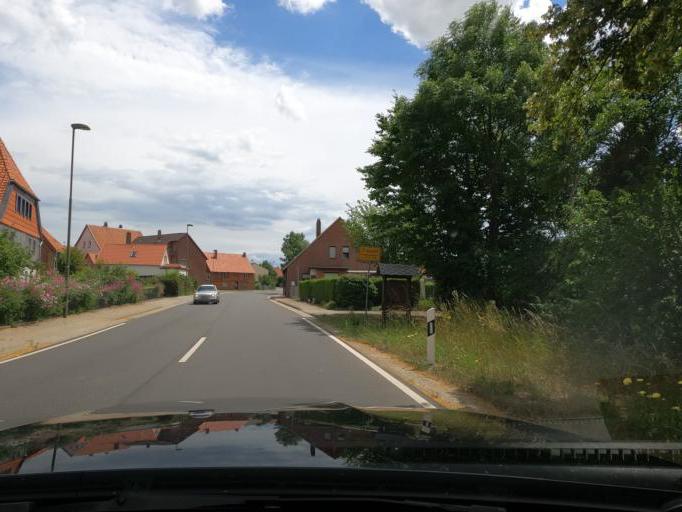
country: DE
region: Lower Saxony
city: Hohenhameln
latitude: 52.2517
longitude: 10.0205
